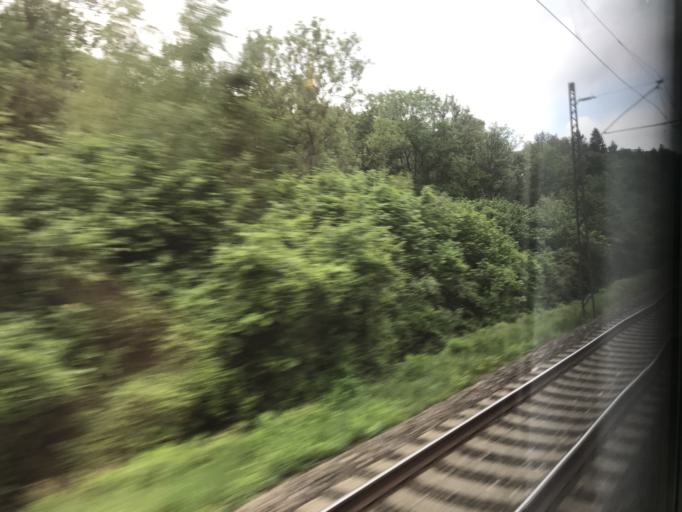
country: DE
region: Bavaria
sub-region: Swabia
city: Leipheim
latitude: 48.4397
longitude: 10.1881
